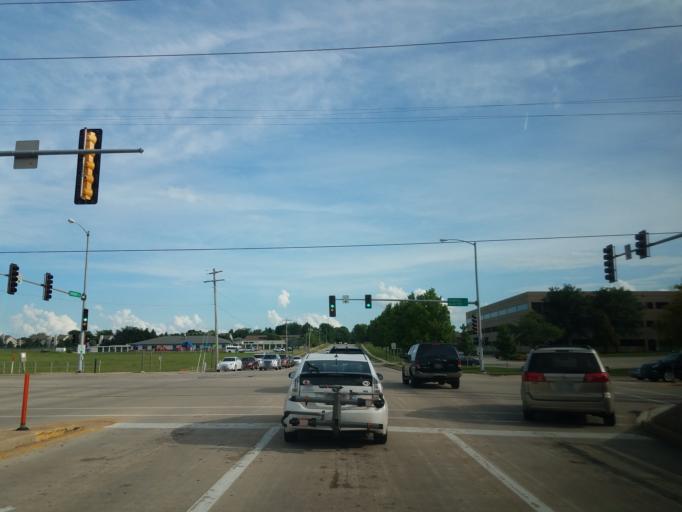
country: US
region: Illinois
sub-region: McLean County
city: Normal
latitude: 40.5030
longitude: -88.9388
